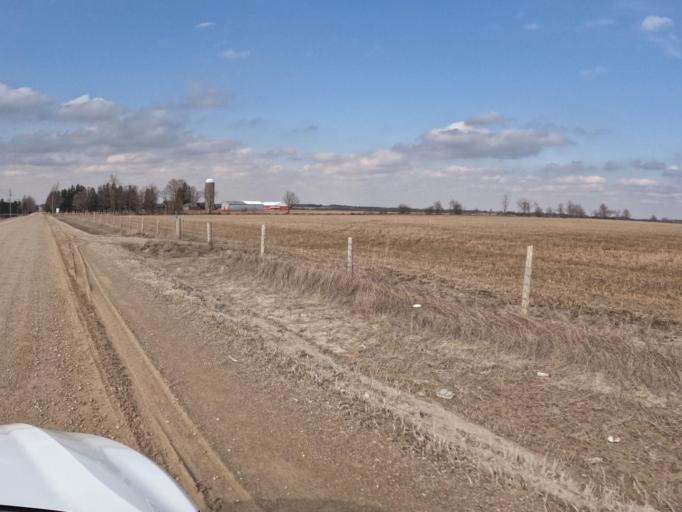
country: CA
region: Ontario
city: Orangeville
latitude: 43.8815
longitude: -80.2970
